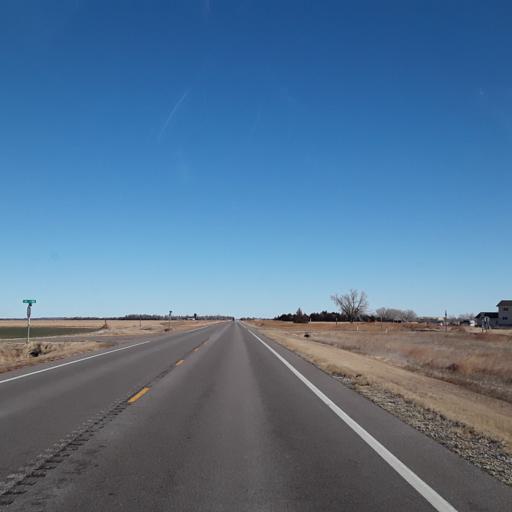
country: US
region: Kansas
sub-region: Pawnee County
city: Larned
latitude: 38.1011
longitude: -99.2064
